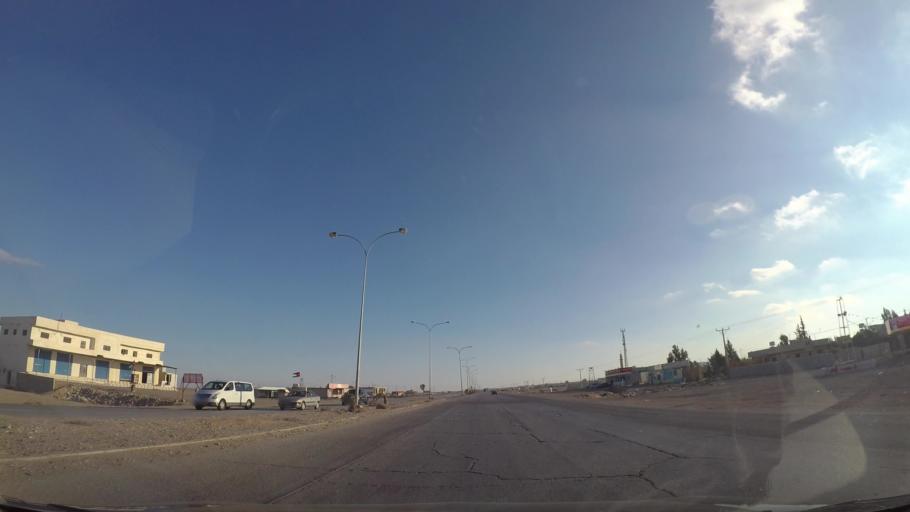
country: JO
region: Tafielah
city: Busayra
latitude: 30.5277
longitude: 35.7994
